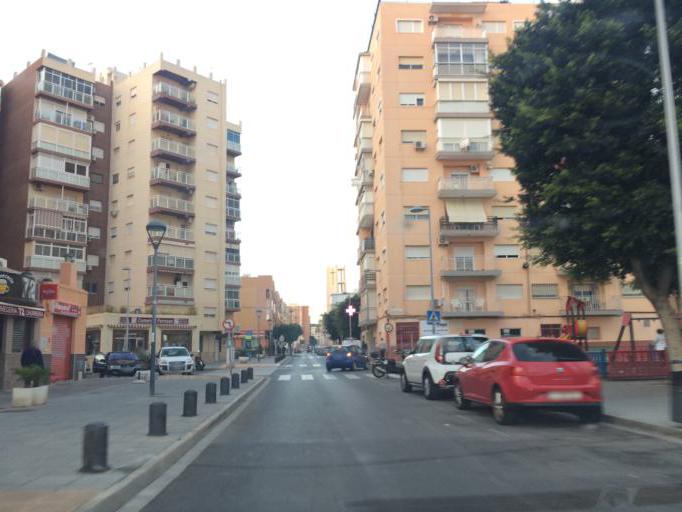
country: ES
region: Andalusia
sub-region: Provincia de Almeria
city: Almeria
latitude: 36.8308
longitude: -2.4490
